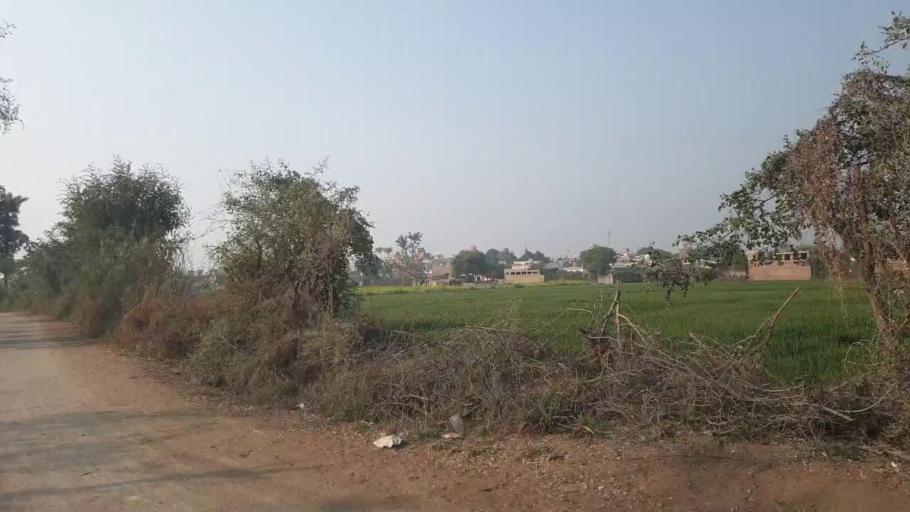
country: PK
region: Sindh
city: Hala
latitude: 25.7867
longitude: 68.3916
